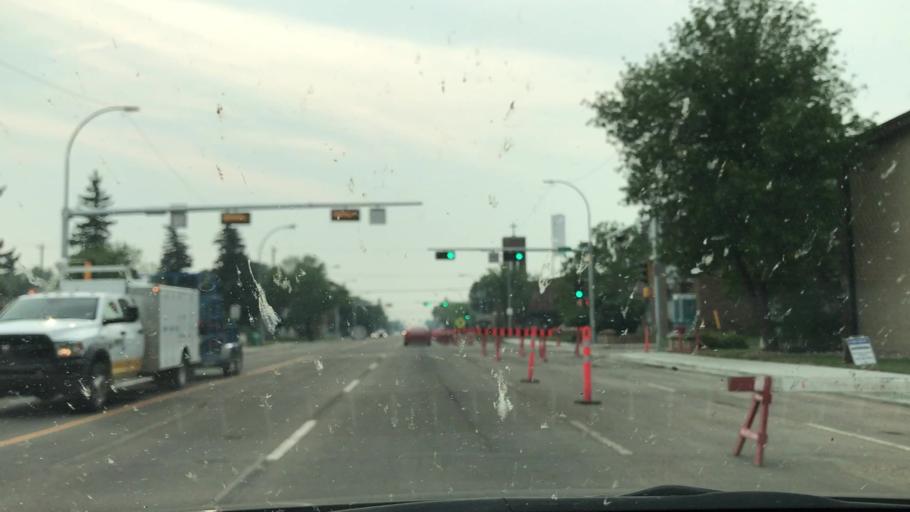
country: CA
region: Alberta
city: Edmonton
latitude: 53.5589
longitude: -113.5405
